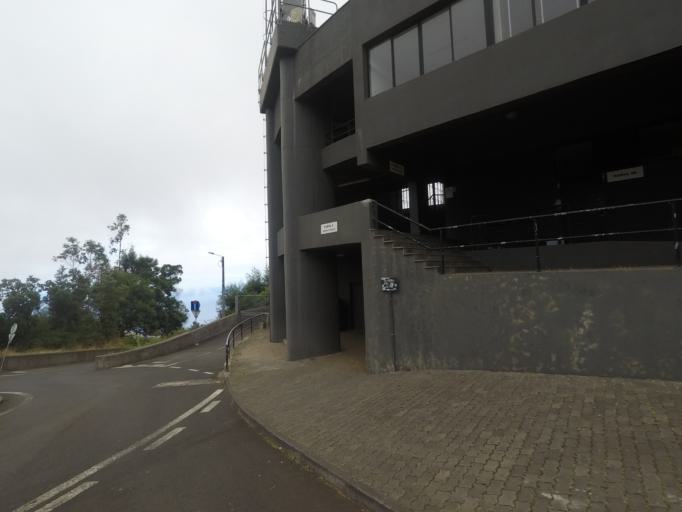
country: PT
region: Madeira
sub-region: Funchal
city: Nossa Senhora do Monte
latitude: 32.6703
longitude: -16.8829
